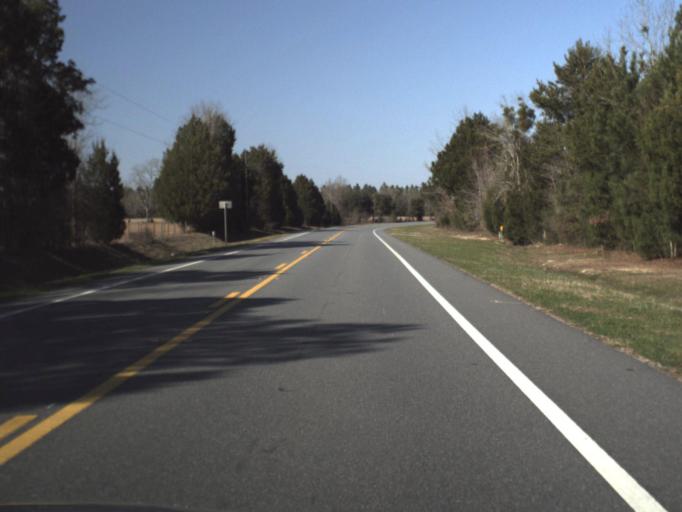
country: US
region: Florida
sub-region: Calhoun County
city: Blountstown
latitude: 30.3991
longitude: -85.2129
